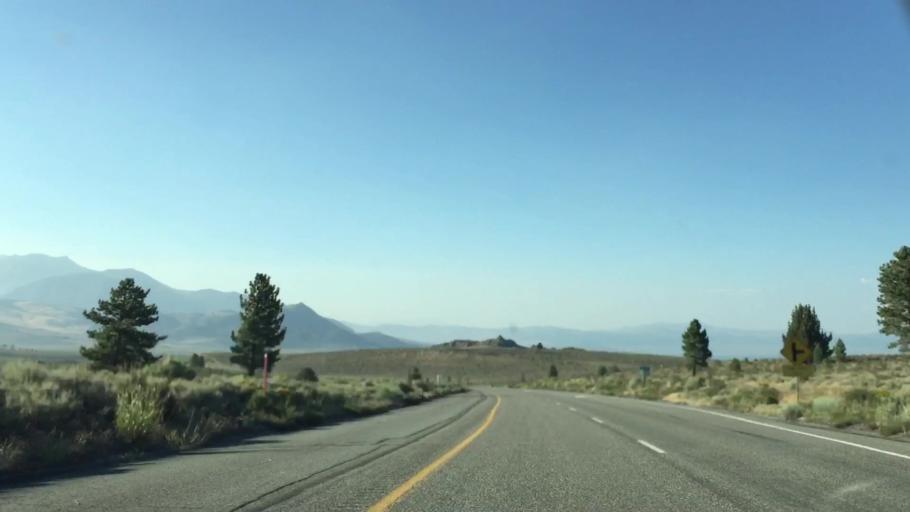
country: US
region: California
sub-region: Mono County
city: Mammoth Lakes
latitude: 37.8378
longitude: -119.0701
